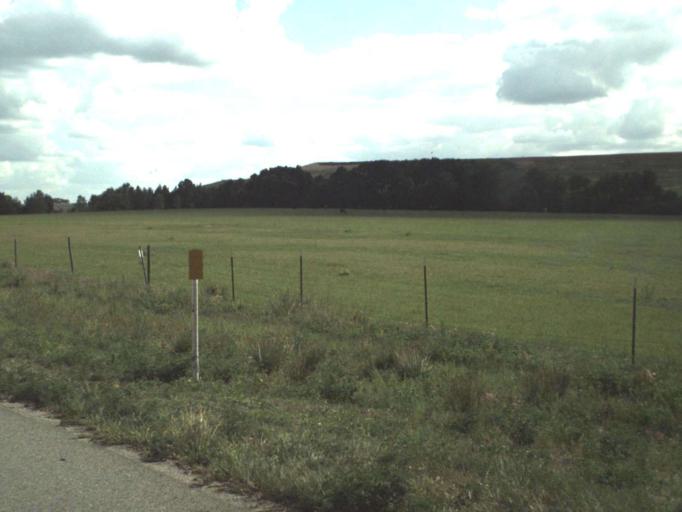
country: US
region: Florida
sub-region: Marion County
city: Silver Springs Shores
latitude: 29.1273
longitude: -82.0537
